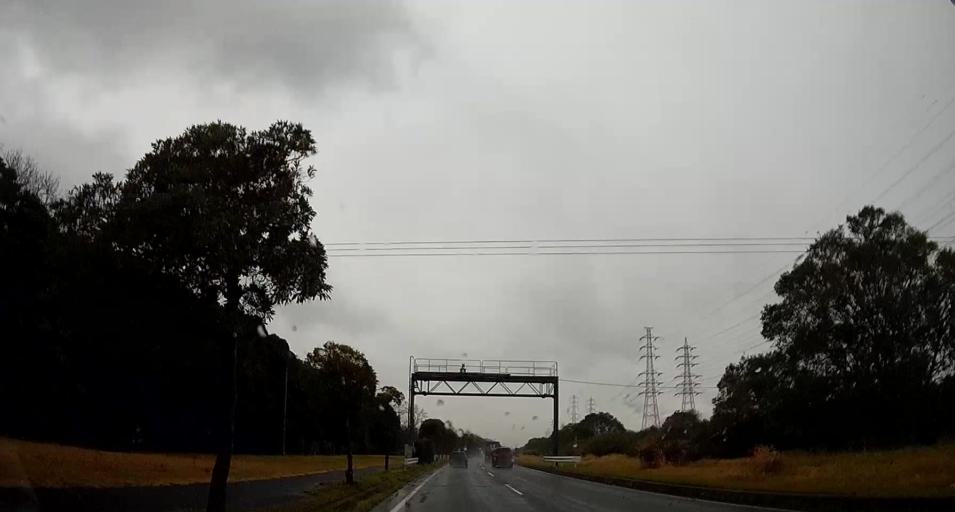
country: JP
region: Chiba
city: Ichihara
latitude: 35.4663
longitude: 140.0230
